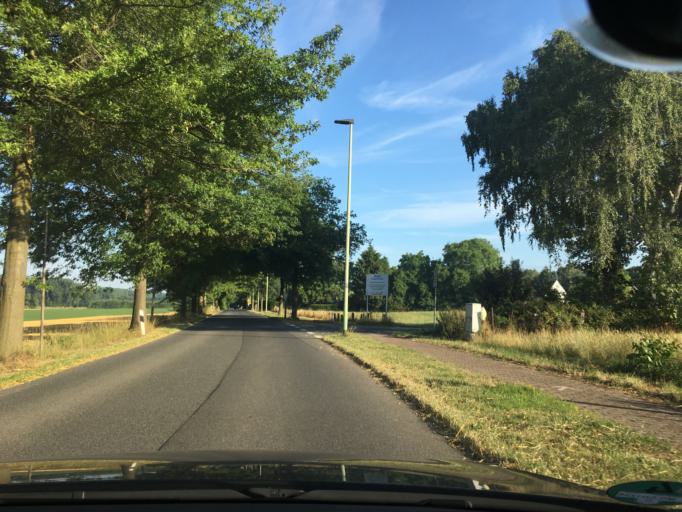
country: DE
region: North Rhine-Westphalia
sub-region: Regierungsbezirk Koln
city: Niederzier
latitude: 50.9046
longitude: 6.4440
